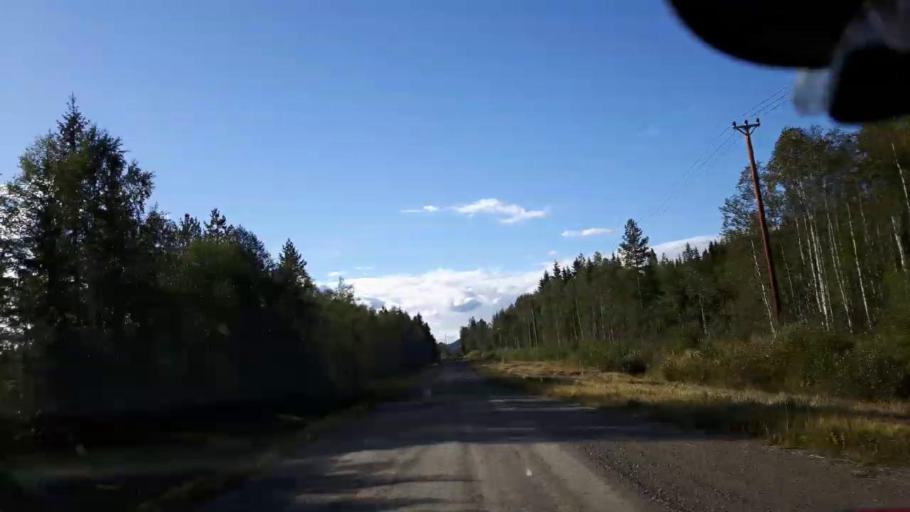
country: SE
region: Jaemtland
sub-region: Ragunda Kommun
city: Hammarstrand
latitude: 63.4905
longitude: 16.0537
